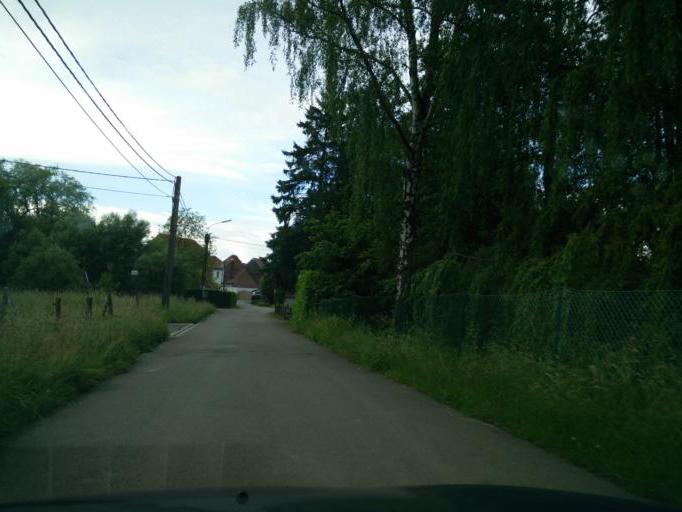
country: BE
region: Flanders
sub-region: Provincie Vlaams-Brabant
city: Beersel
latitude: 50.7195
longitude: 4.3104
